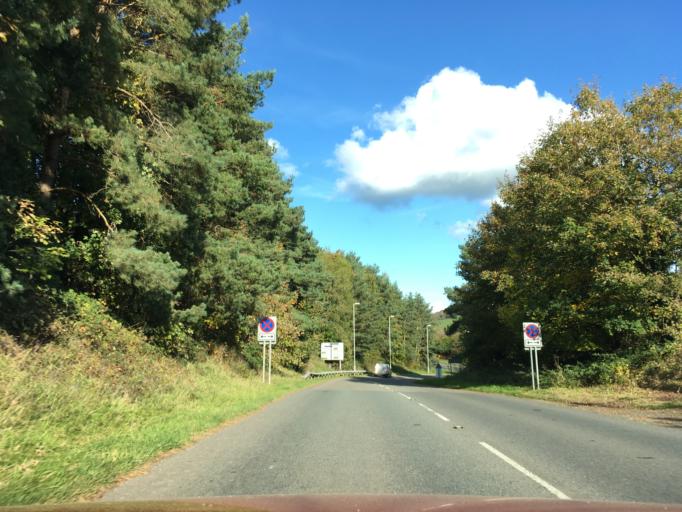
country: GB
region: Wales
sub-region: Sir Powys
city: Brecon
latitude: 51.9630
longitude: -3.3557
